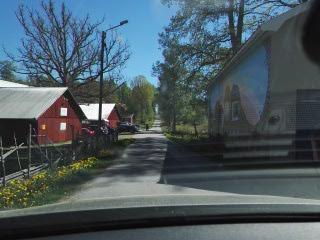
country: SE
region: Kronoberg
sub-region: Vaxjo Kommun
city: Rottne
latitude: 57.0919
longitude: 14.7916
